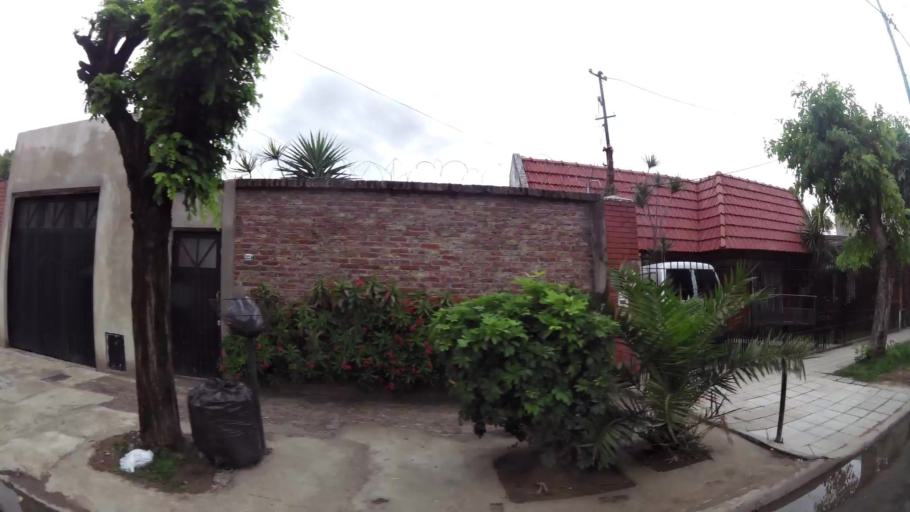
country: AR
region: Buenos Aires
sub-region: Partido de Lomas de Zamora
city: Lomas de Zamora
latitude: -34.7372
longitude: -58.3727
